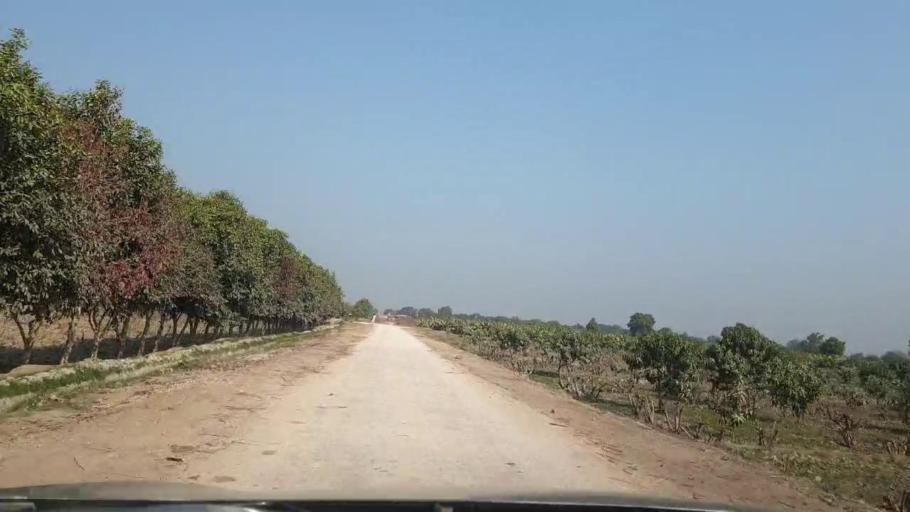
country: PK
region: Sindh
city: Tando Allahyar
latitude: 25.5168
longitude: 68.7631
